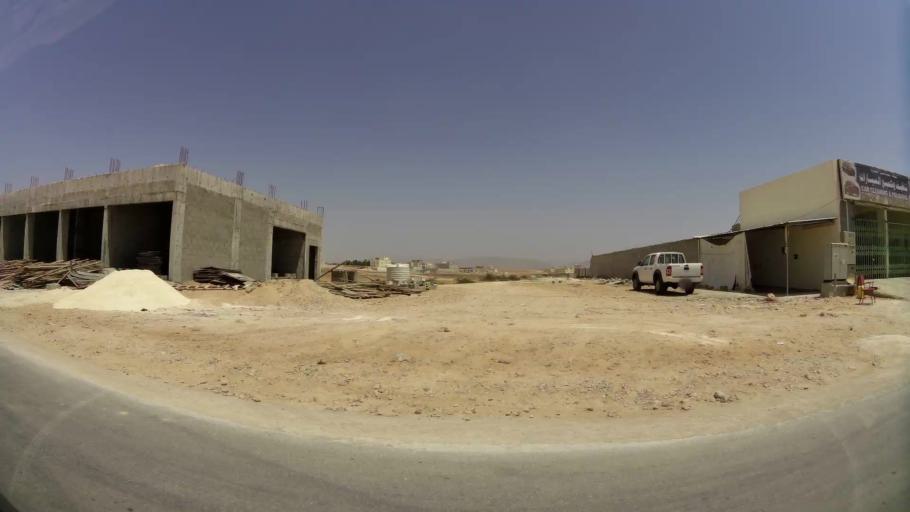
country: OM
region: Zufar
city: Salalah
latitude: 17.0842
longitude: 54.1932
